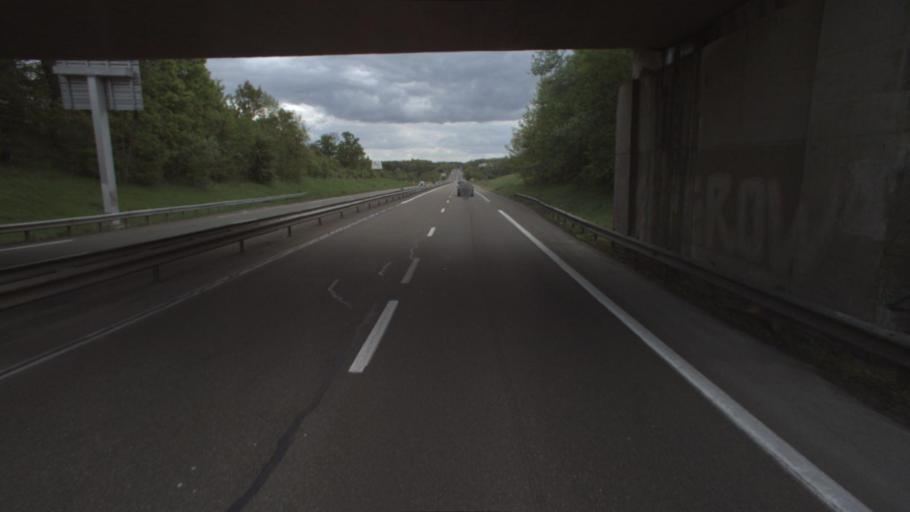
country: FR
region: Ile-de-France
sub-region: Departement de Seine-et-Marne
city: Quincy-Voisins
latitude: 48.9070
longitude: 2.8855
